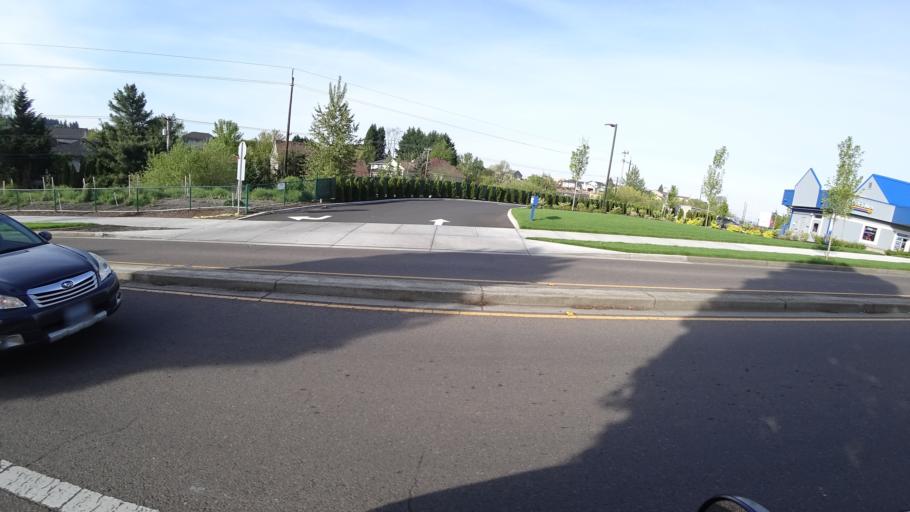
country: US
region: Oregon
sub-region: Washington County
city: King City
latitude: 45.4272
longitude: -122.8456
